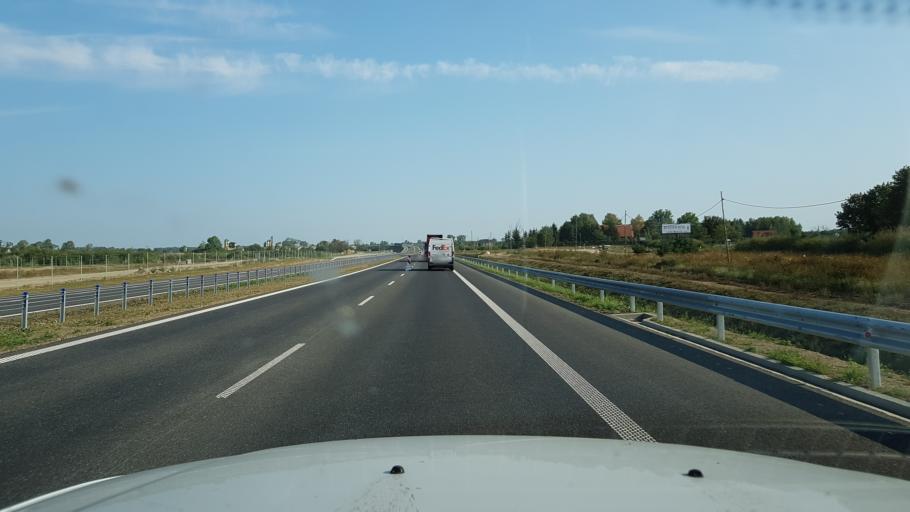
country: PL
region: West Pomeranian Voivodeship
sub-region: Powiat gryficki
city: Ploty
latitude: 53.7885
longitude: 15.2512
